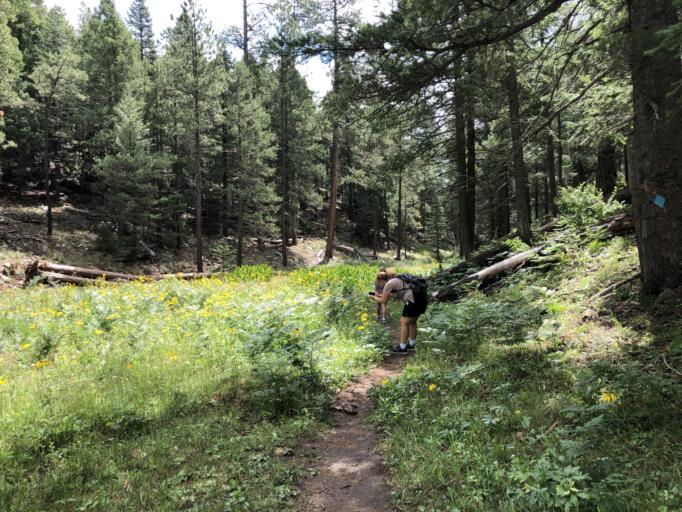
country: US
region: Arizona
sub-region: Gila County
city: Star Valley
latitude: 34.3400
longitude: -110.9560
